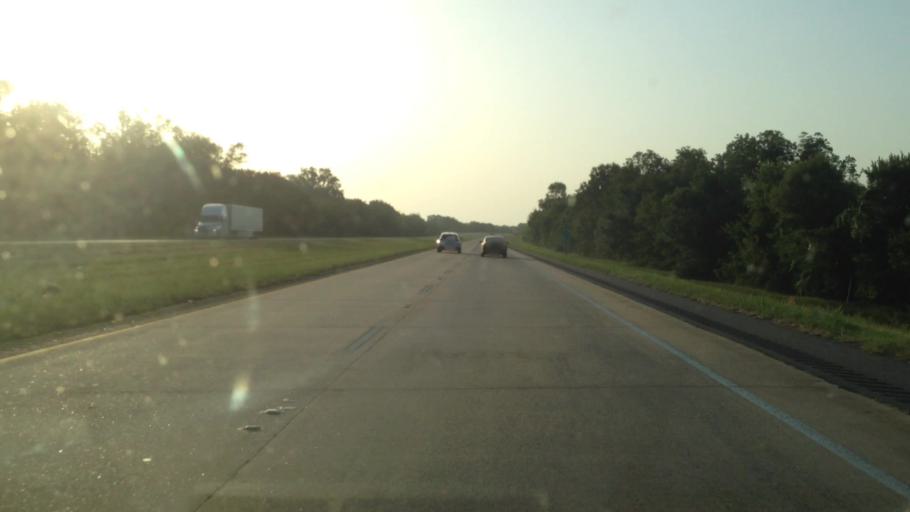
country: US
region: Louisiana
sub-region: Natchitoches Parish
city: Vienna Bend
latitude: 31.5692
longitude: -93.0052
